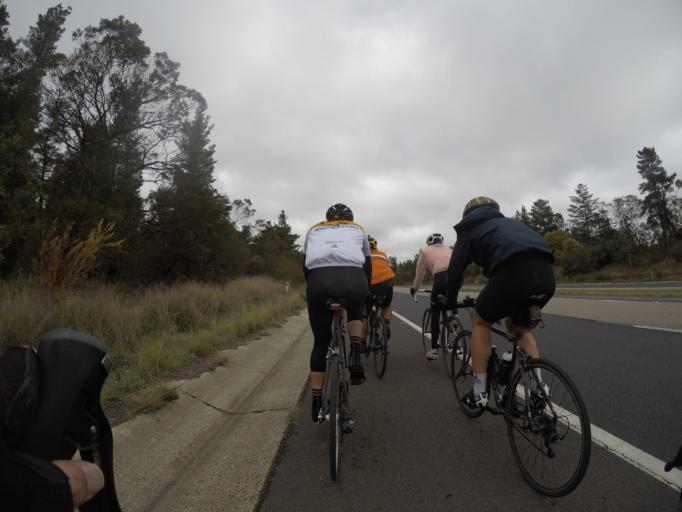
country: AU
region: New South Wales
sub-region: Lithgow
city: Lithgow
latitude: -33.4388
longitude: 150.0620
